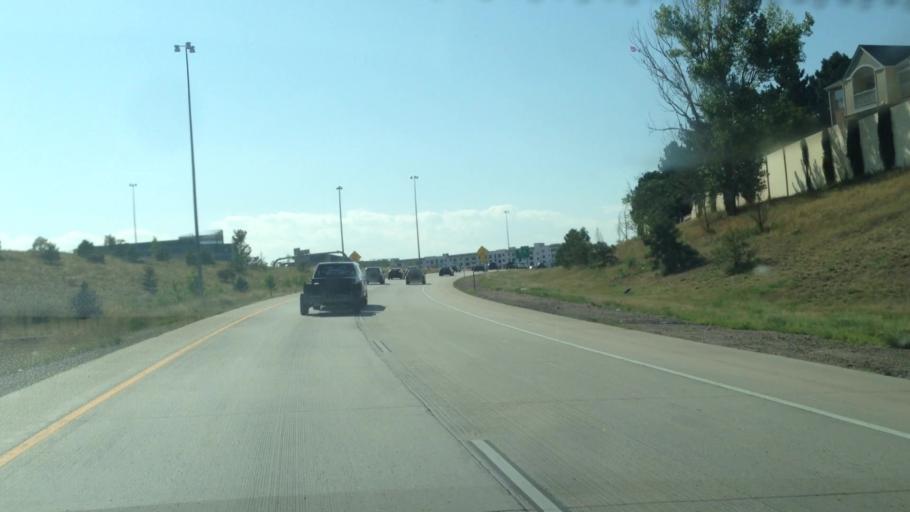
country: US
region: Colorado
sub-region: Arapahoe County
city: Greenwood Village
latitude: 39.6355
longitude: -104.9051
